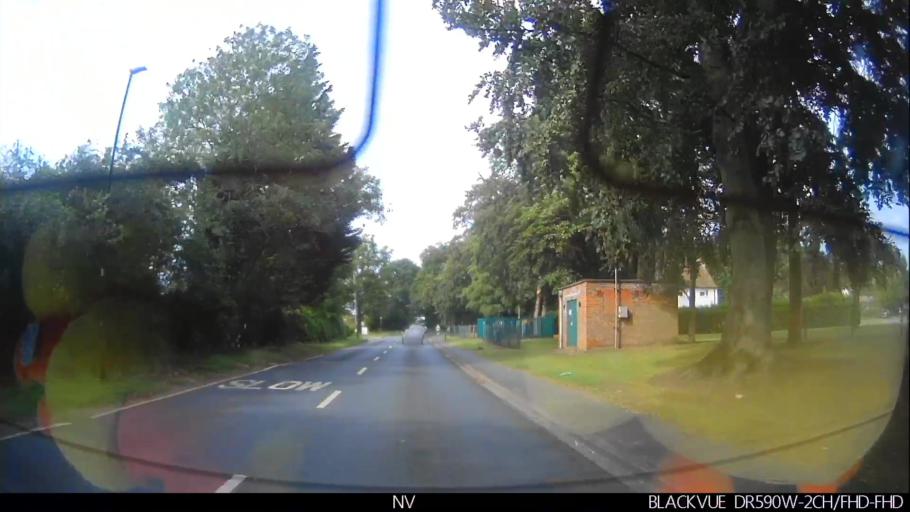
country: GB
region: England
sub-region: North Yorkshire
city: Strensall
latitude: 54.0226
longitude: -1.0445
